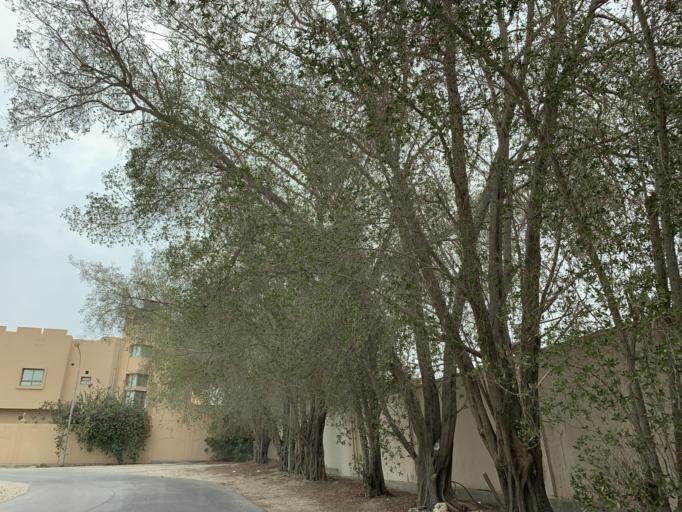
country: BH
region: Central Governorate
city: Madinat Hamad
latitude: 26.1783
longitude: 50.4722
